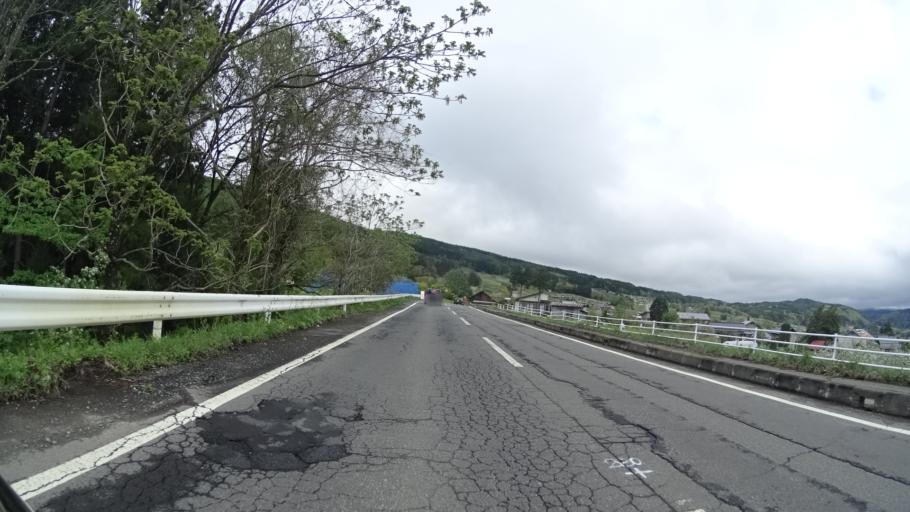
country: JP
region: Nagano
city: Nagano-shi
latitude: 36.7346
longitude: 138.2066
